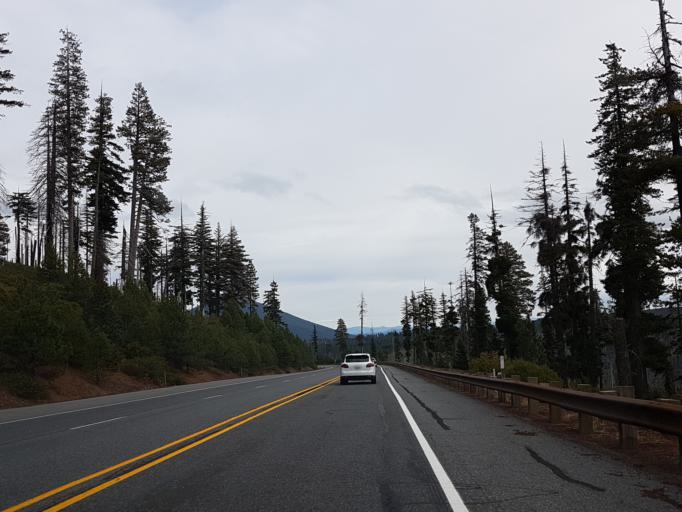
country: US
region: Oregon
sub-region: Deschutes County
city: Sisters
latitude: 44.4200
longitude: -121.7871
